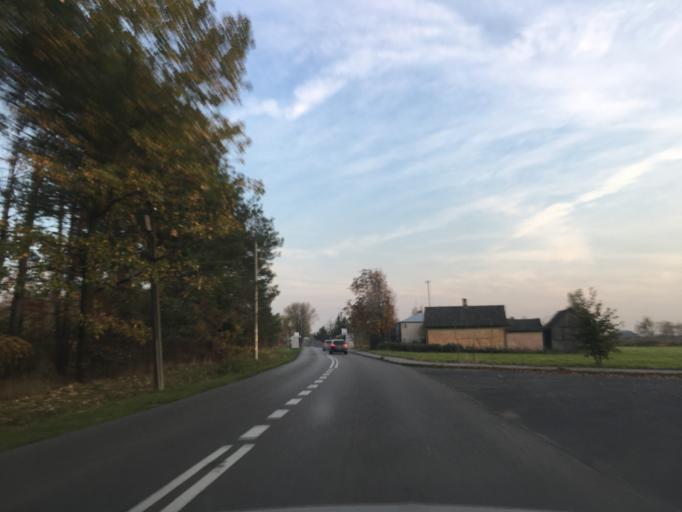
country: PL
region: Masovian Voivodeship
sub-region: Powiat piaseczynski
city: Lesznowola
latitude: 52.0557
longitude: 20.9236
